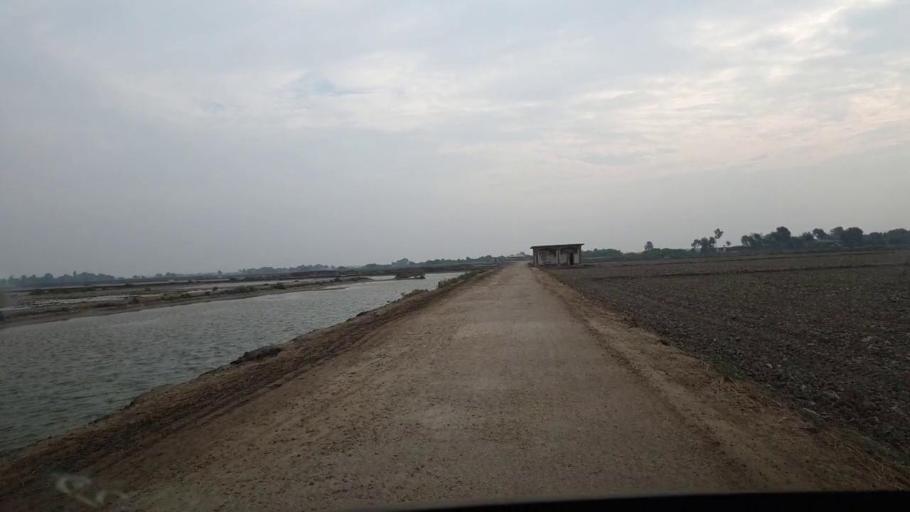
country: PK
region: Sindh
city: Chuhar Jamali
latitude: 24.4131
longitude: 67.9987
